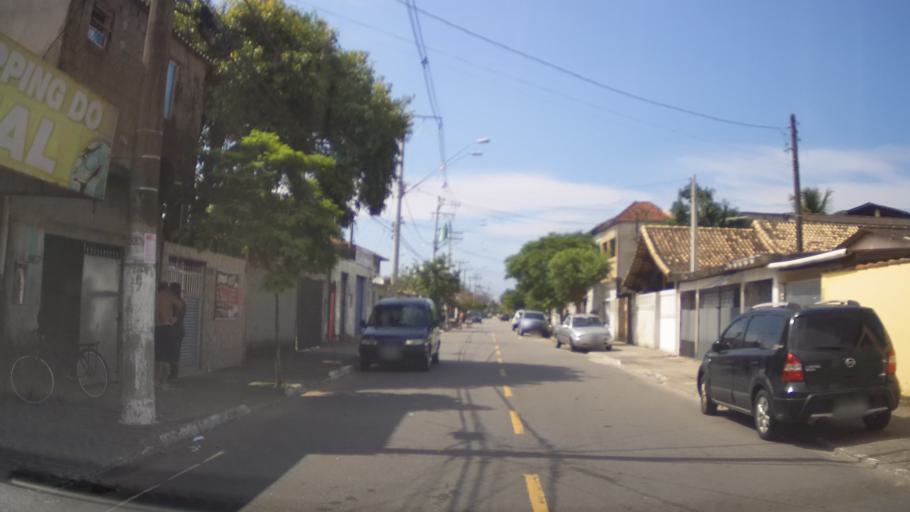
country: BR
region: Sao Paulo
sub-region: Praia Grande
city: Praia Grande
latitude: -24.0196
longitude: -46.4862
